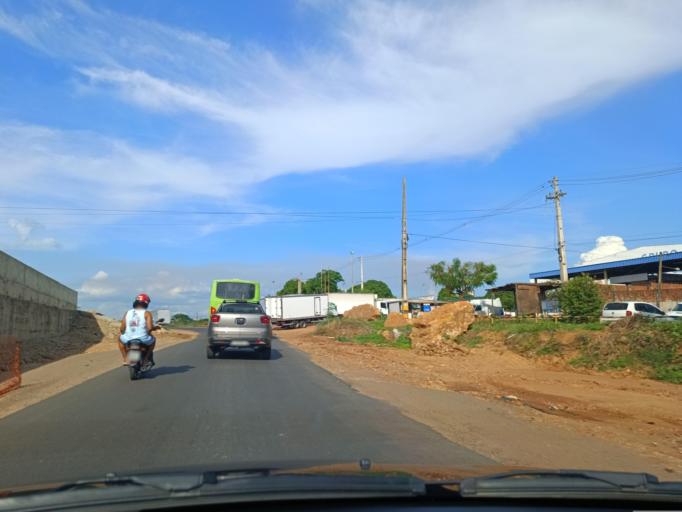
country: BR
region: Piaui
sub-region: Teresina
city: Teresina
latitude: -5.0894
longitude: -42.7596
